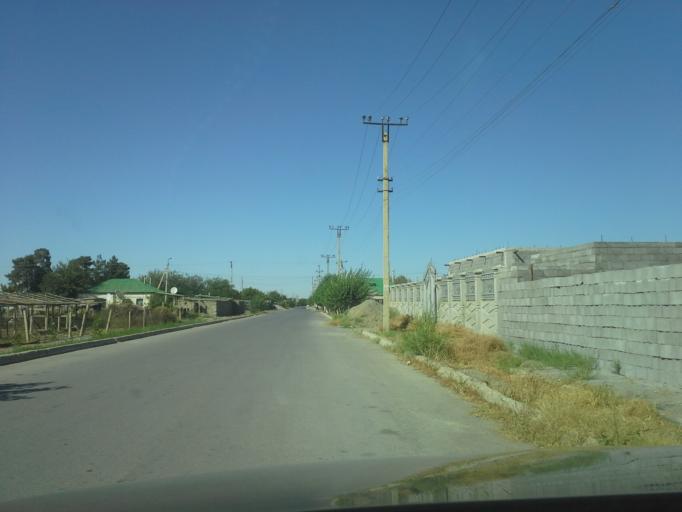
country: TM
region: Ahal
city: Abadan
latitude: 38.0806
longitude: 58.1608
